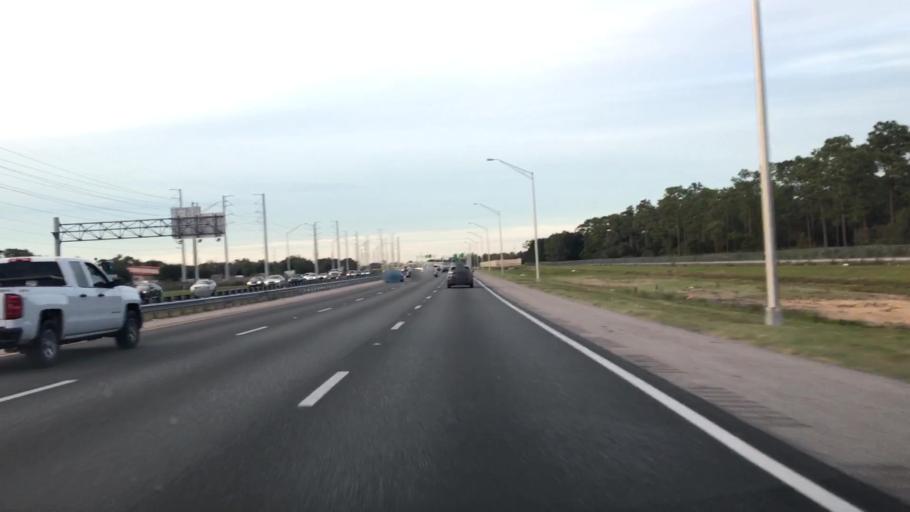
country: US
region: Florida
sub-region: Orange County
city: Azalea Park
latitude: 28.5283
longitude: -81.2507
